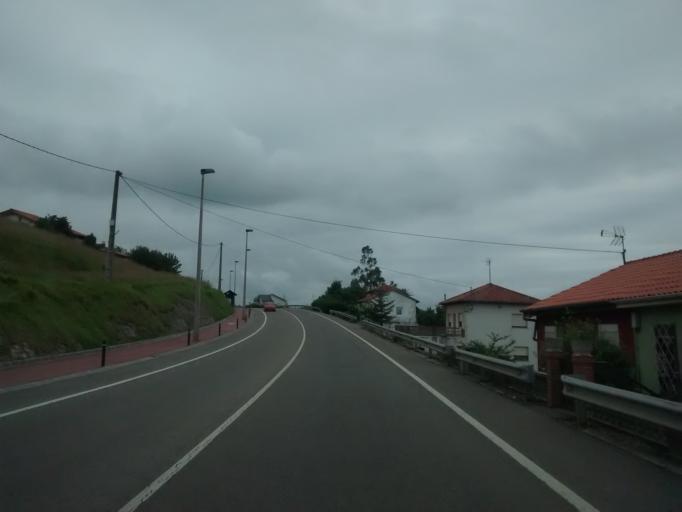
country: ES
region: Cantabria
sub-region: Provincia de Cantabria
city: Suances
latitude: 43.4058
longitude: -4.0449
